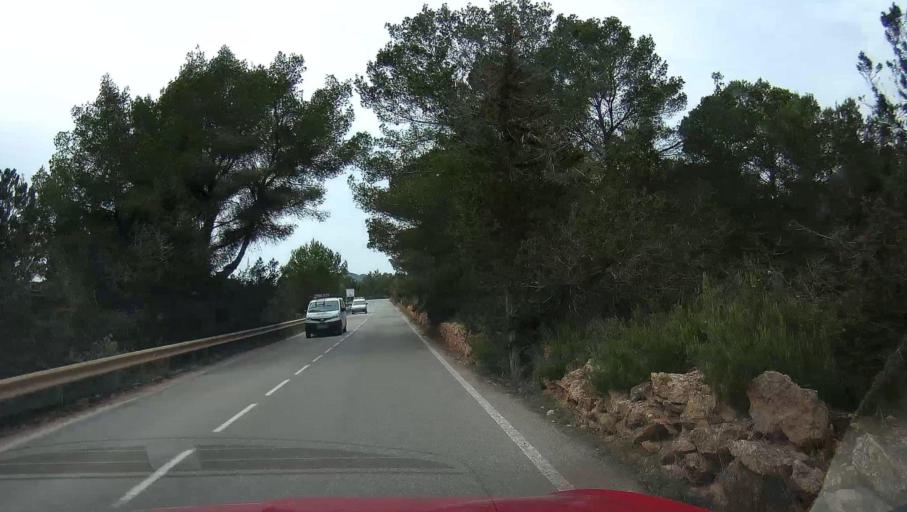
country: ES
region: Balearic Islands
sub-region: Illes Balears
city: Sant Josep de sa Talaia
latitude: 38.8694
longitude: 1.3351
